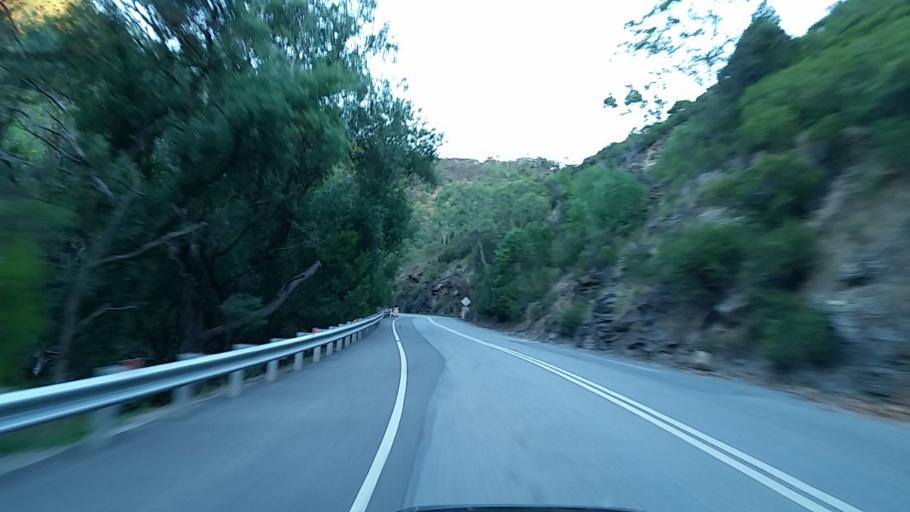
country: AU
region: South Australia
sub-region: Campbelltown
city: Athelstone
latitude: -34.8623
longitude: 138.7428
